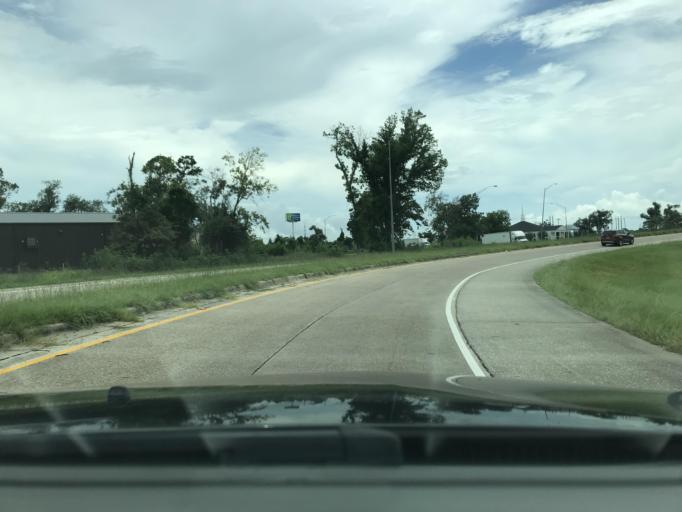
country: US
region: Louisiana
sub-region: Calcasieu Parish
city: Lake Charles
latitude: 30.2452
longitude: -93.1790
